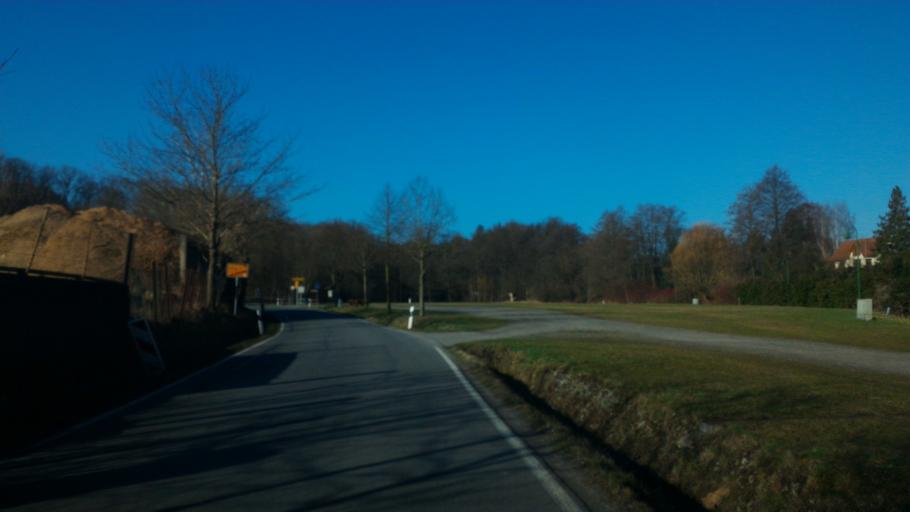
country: DE
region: Saxony
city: Durrrohrsdorf
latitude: 51.0357
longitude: 13.9866
